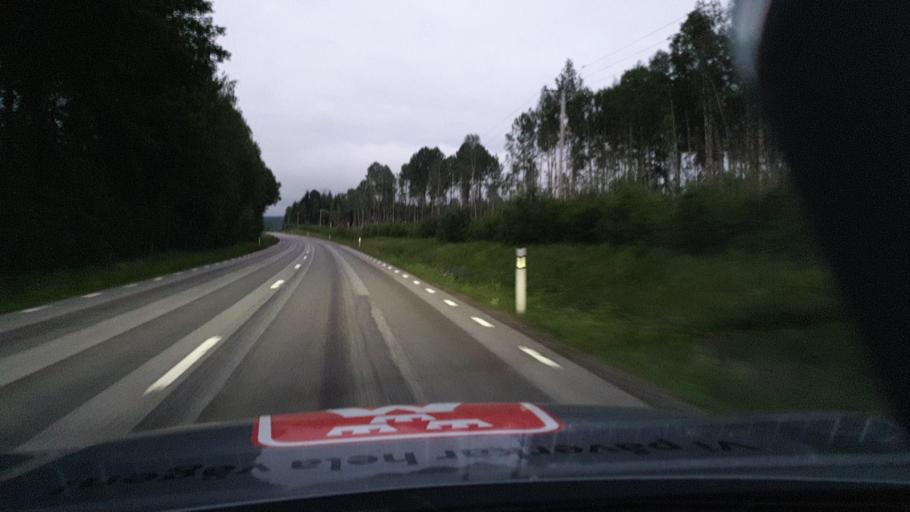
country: SE
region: OErebro
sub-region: Hallefors Kommun
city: Haellefors
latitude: 59.7753
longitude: 14.3901
